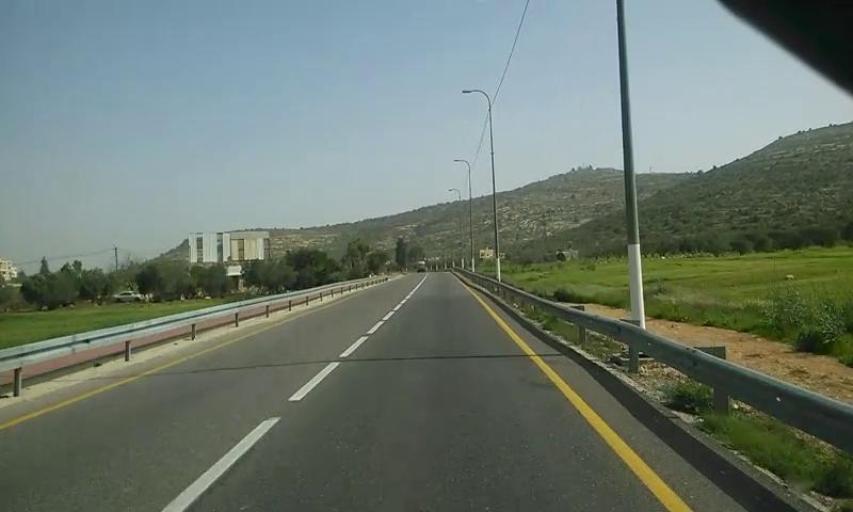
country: PS
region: West Bank
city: As Sawiyah
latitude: 32.0851
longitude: 35.2647
